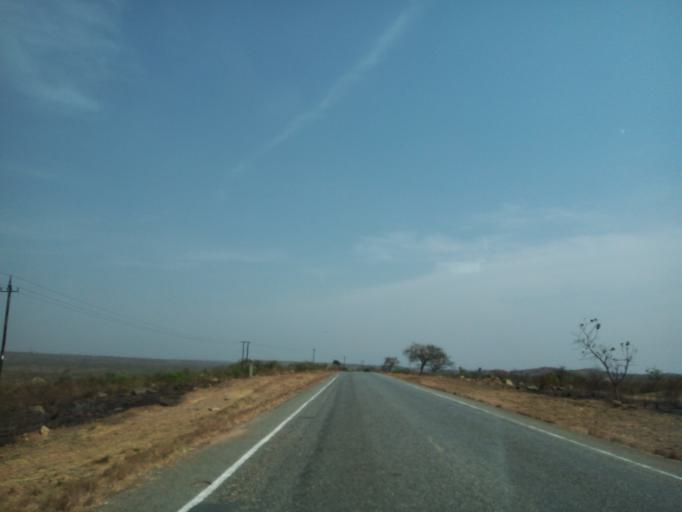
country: UG
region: Northern Region
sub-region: Nebbi District
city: Nebbi
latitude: 2.4424
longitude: 31.2528
